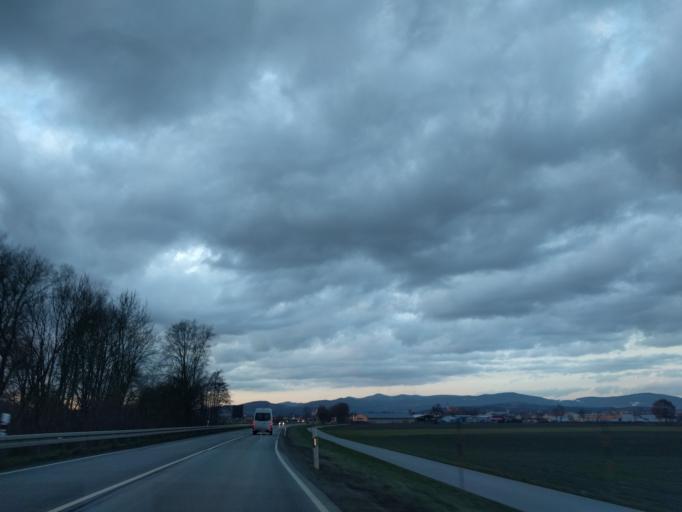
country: DE
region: Bavaria
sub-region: Lower Bavaria
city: Hengersberg
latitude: 48.7551
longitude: 13.0544
